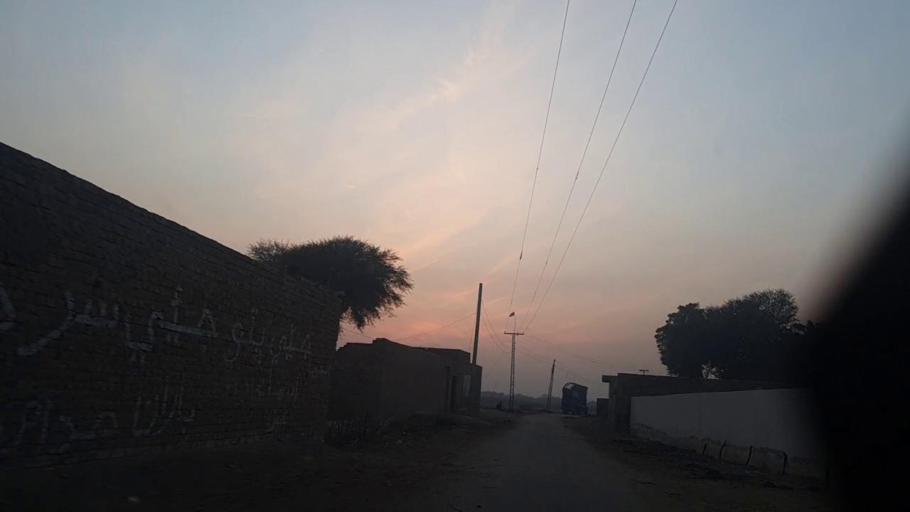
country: PK
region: Sindh
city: Sakrand
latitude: 26.1009
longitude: 68.3137
